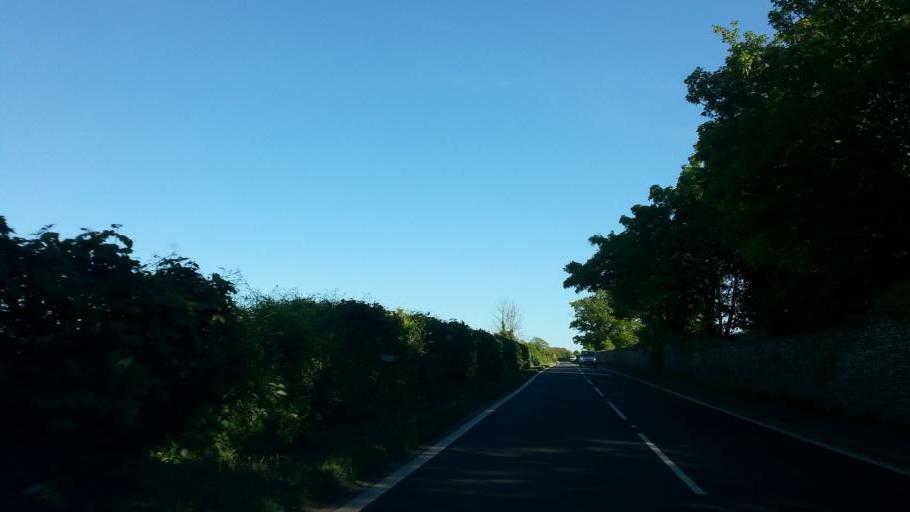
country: GB
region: England
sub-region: Dorset
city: Stalbridge
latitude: 50.9672
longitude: -2.3858
